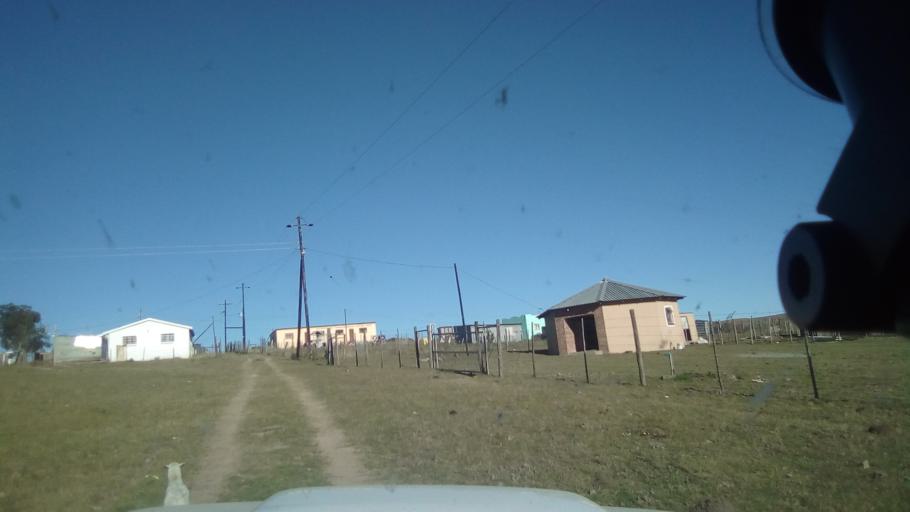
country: ZA
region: Eastern Cape
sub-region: Buffalo City Metropolitan Municipality
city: Bhisho
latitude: -32.9485
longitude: 27.2902
